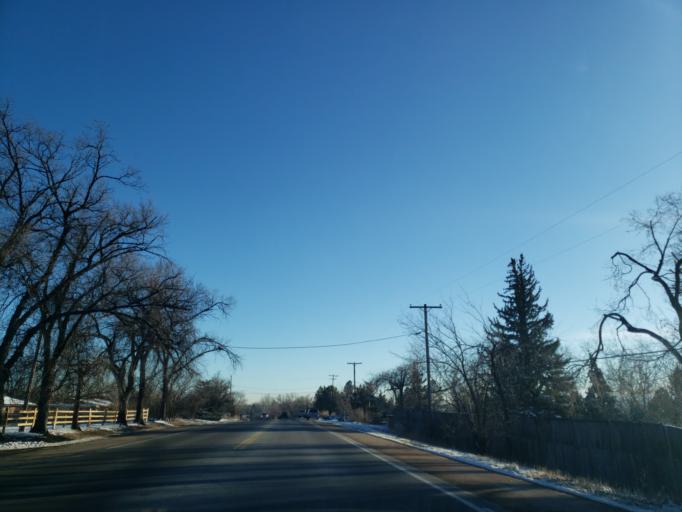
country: US
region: Colorado
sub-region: Larimer County
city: Fort Collins
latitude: 40.6354
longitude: -105.0723
